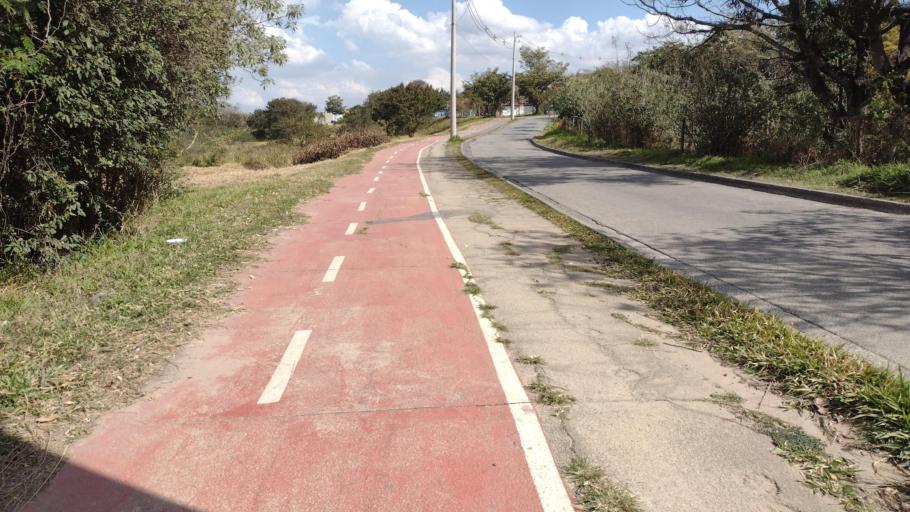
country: BR
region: Sao Paulo
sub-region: Sorocaba
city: Sorocaba
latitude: -23.4414
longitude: -47.4624
